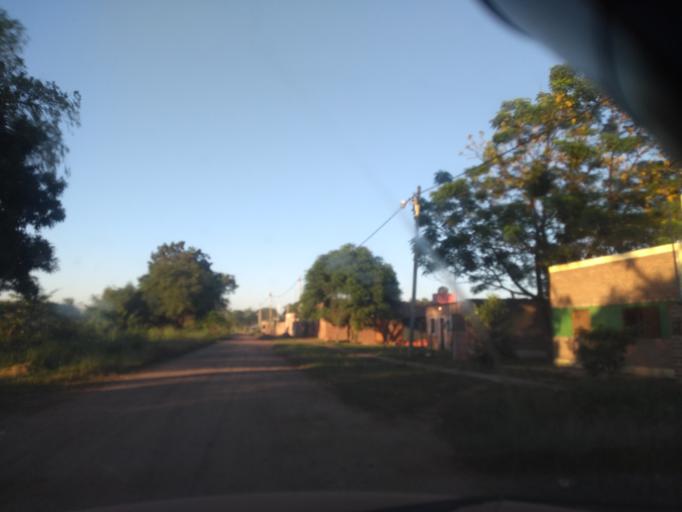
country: AR
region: Chaco
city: Resistencia
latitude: -27.4571
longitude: -58.9678
